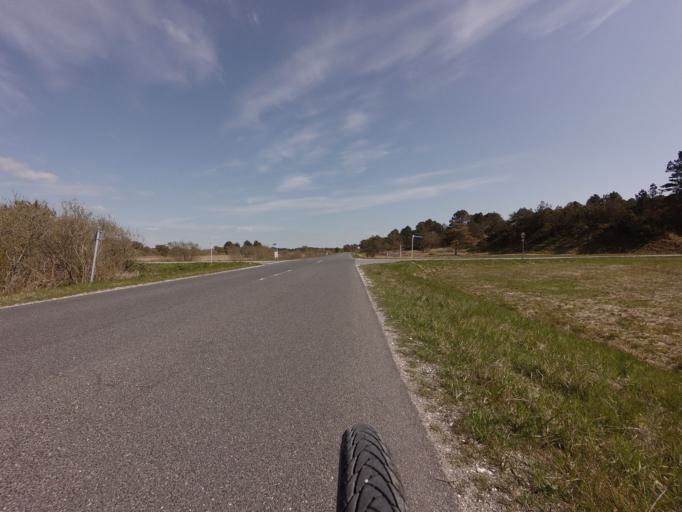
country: DK
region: North Denmark
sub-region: Jammerbugt Kommune
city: Brovst
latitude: 57.2008
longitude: 9.5490
